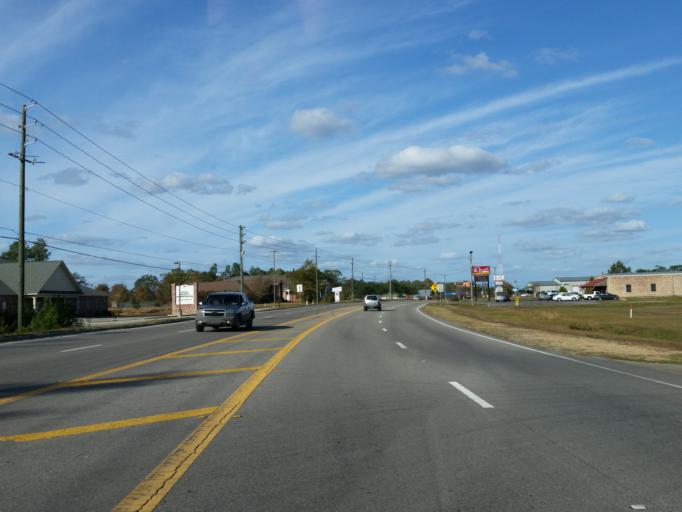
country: US
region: Mississippi
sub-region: Forrest County
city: Hattiesburg
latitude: 31.2963
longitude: -89.3242
